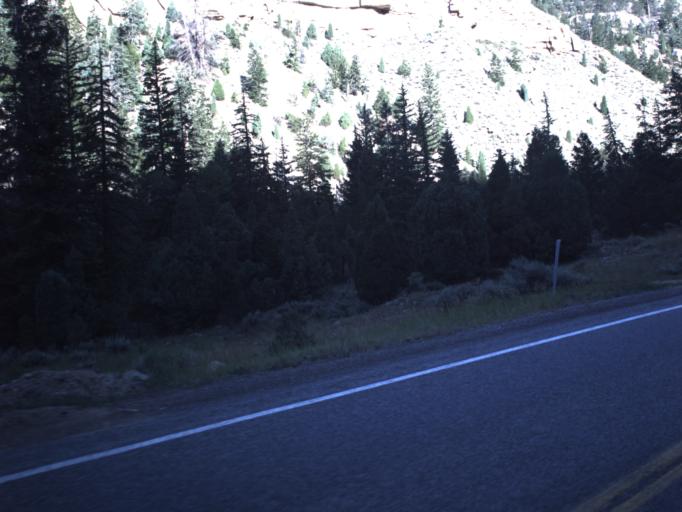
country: US
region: Utah
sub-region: Emery County
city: Huntington
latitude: 39.4345
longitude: -111.1312
